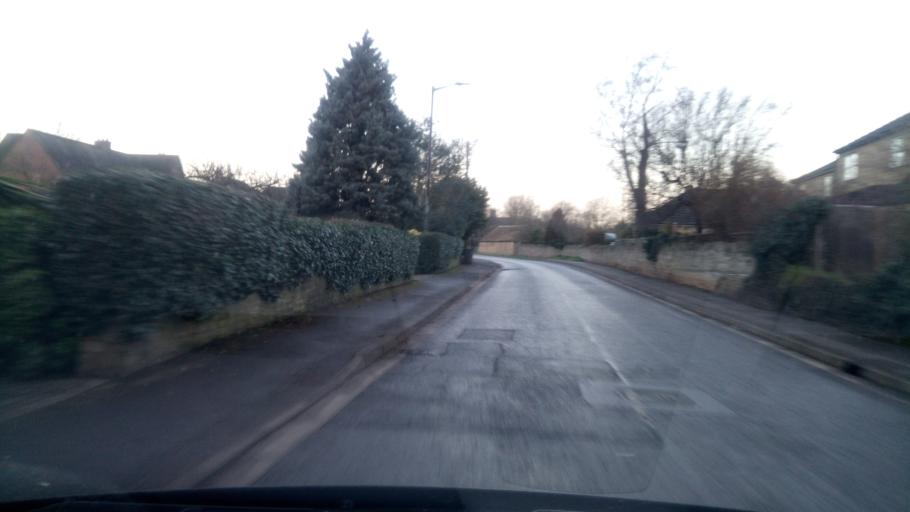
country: GB
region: England
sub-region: Peterborough
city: Castor
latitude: 52.5733
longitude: -0.3472
